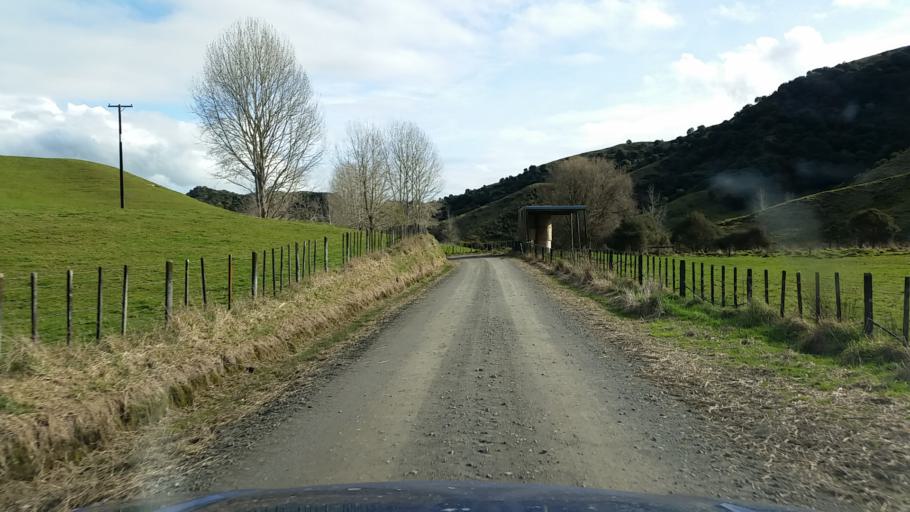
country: NZ
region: Taranaki
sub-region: South Taranaki District
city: Eltham
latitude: -39.2598
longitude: 174.5874
